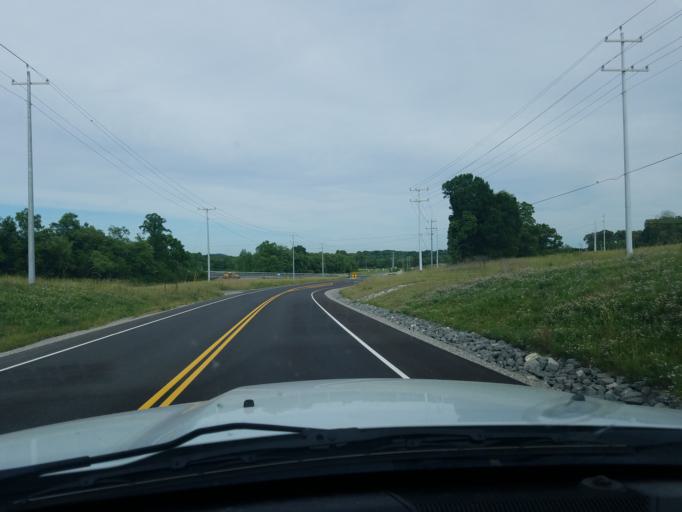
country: US
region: Tennessee
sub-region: Putnam County
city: Baxter
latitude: 36.1368
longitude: -85.5828
